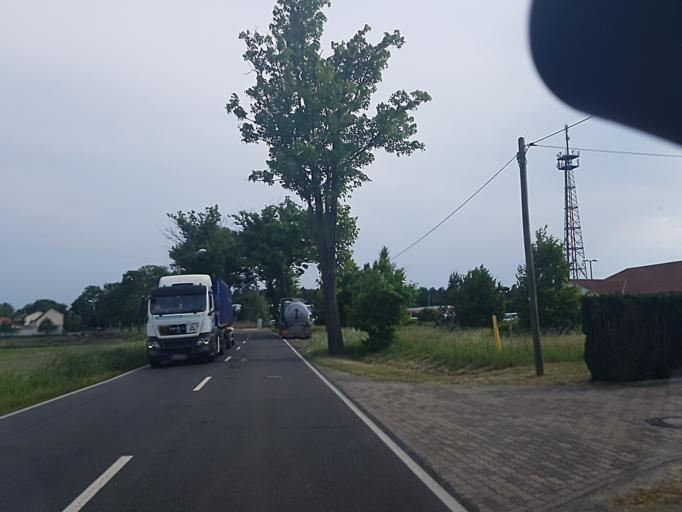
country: DE
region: Saxony-Anhalt
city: Nudersdorf
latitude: 51.9122
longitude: 12.6065
